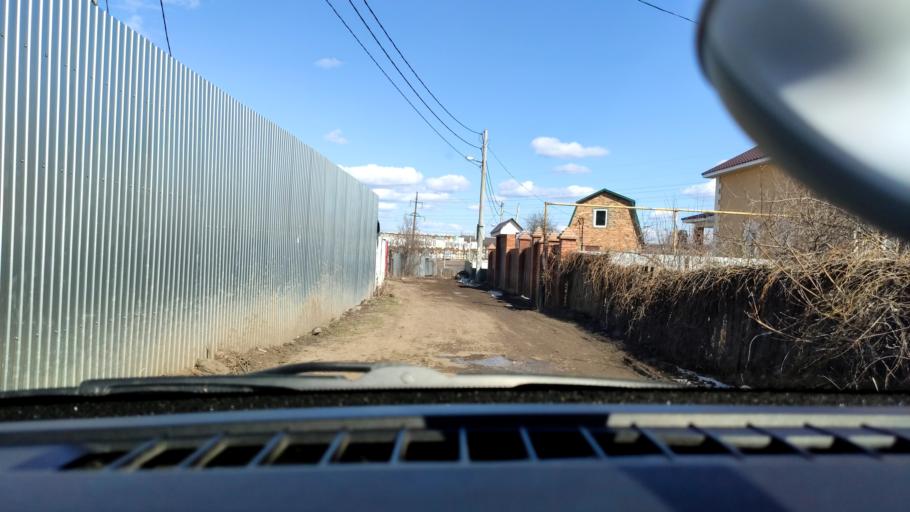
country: RU
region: Samara
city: Petra-Dubrava
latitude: 53.2917
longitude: 50.3118
